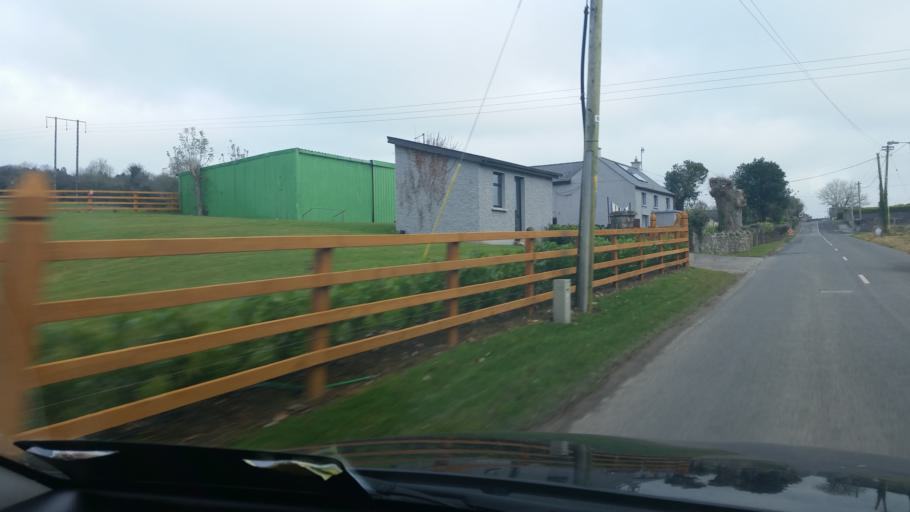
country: IE
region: Leinster
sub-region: An Mhi
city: Duleek
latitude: 53.6926
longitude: -6.4232
